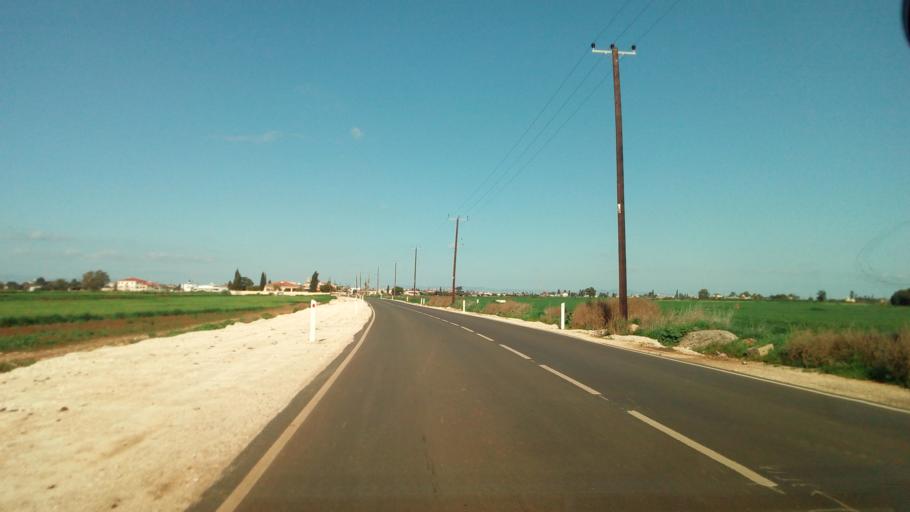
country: CY
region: Ammochostos
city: Avgorou
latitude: 35.0177
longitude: 33.8427
